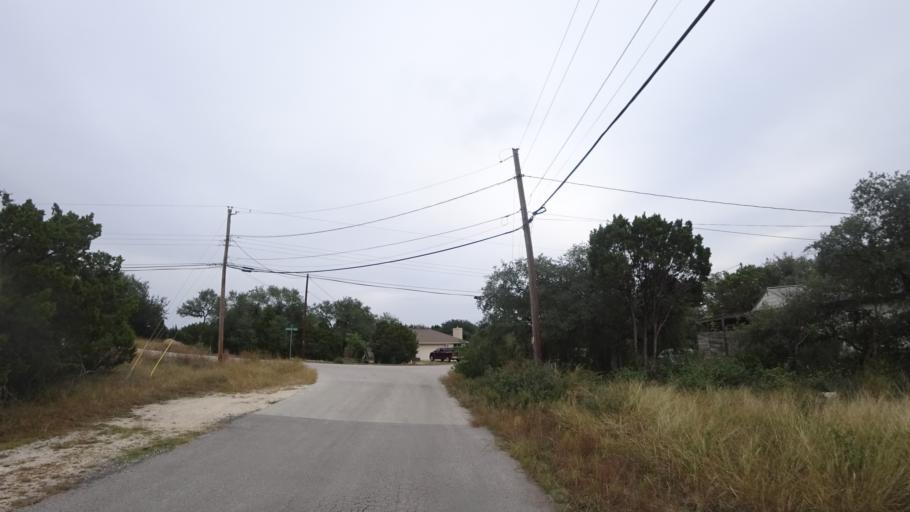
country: US
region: Texas
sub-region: Travis County
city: Hudson Bend
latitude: 30.3722
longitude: -97.9249
